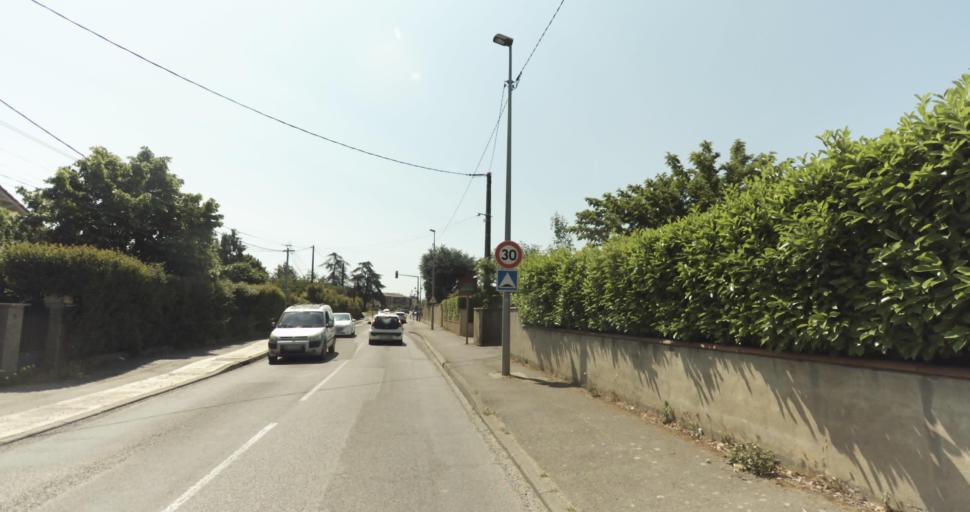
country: FR
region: Midi-Pyrenees
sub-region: Departement de la Haute-Garonne
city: Plaisance-du-Touch
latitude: 43.5696
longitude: 1.2947
